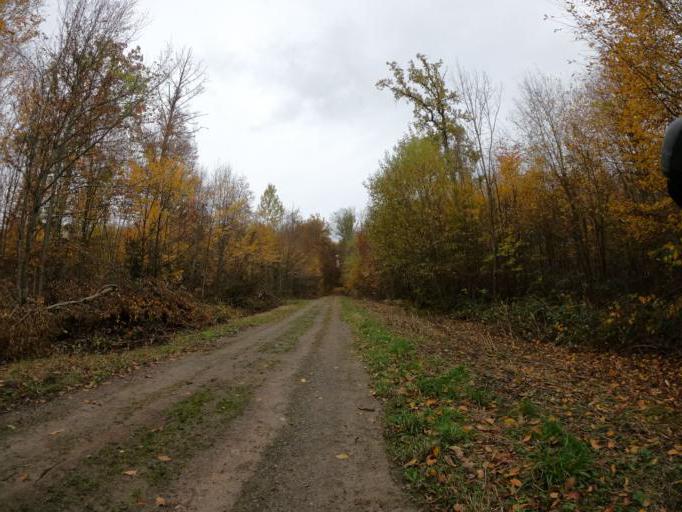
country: DE
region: Baden-Wuerttemberg
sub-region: Regierungsbezirk Stuttgart
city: Hildrizhausen
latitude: 48.6380
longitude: 8.9505
